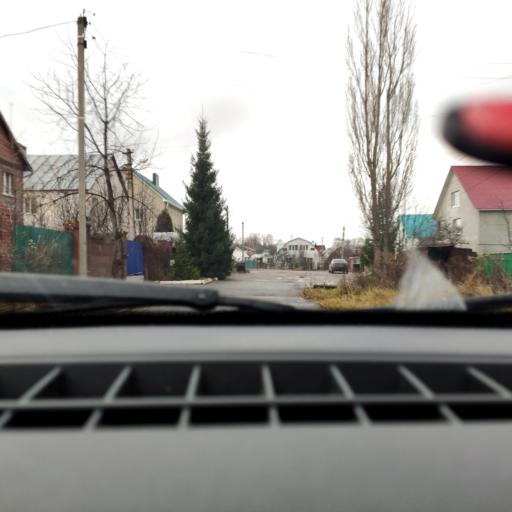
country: RU
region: Bashkortostan
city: Mikhaylovka
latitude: 54.7920
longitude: 55.9412
